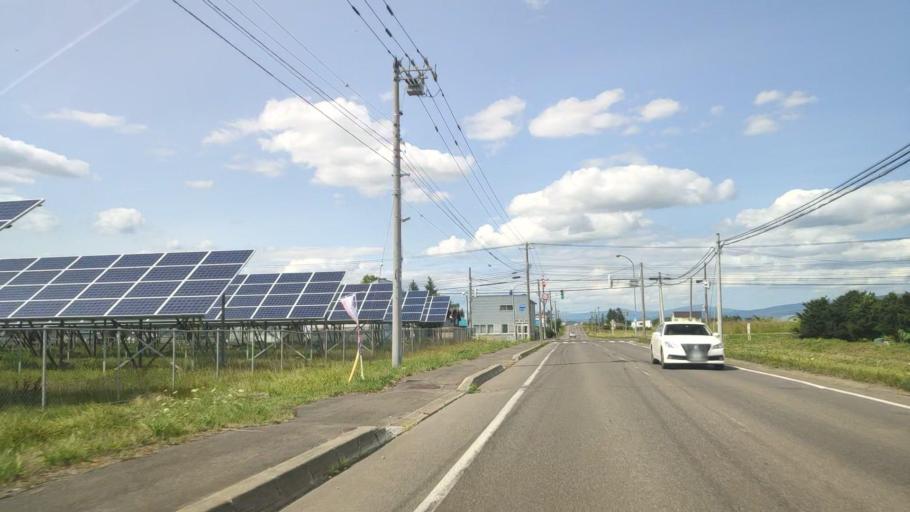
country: JP
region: Hokkaido
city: Nayoro
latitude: 44.2955
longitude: 142.4294
